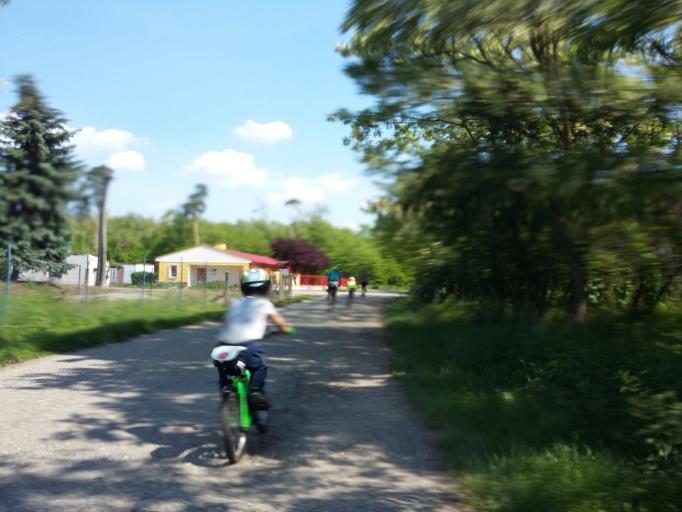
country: AT
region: Lower Austria
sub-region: Politischer Bezirk Ganserndorf
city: Drosing
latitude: 48.5080
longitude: 16.9641
